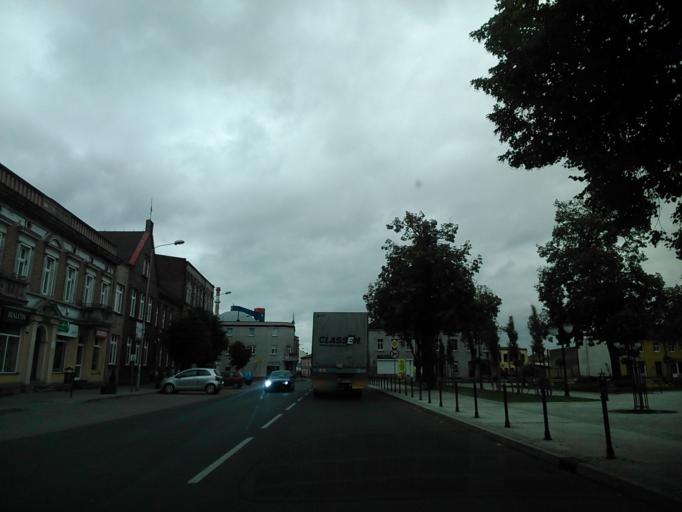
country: PL
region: Kujawsko-Pomorskie
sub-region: Powiat inowroclawski
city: Kruszwica
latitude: 52.6736
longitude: 18.3214
